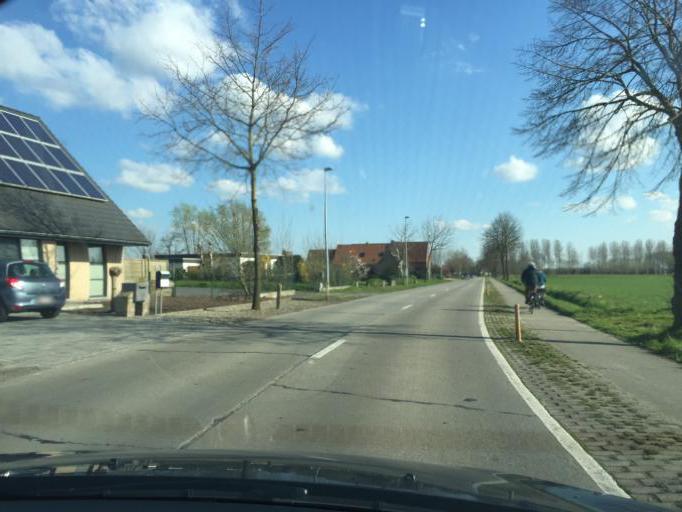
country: BE
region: Flanders
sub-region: Provincie West-Vlaanderen
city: Beernem
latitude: 51.1636
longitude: 3.3154
